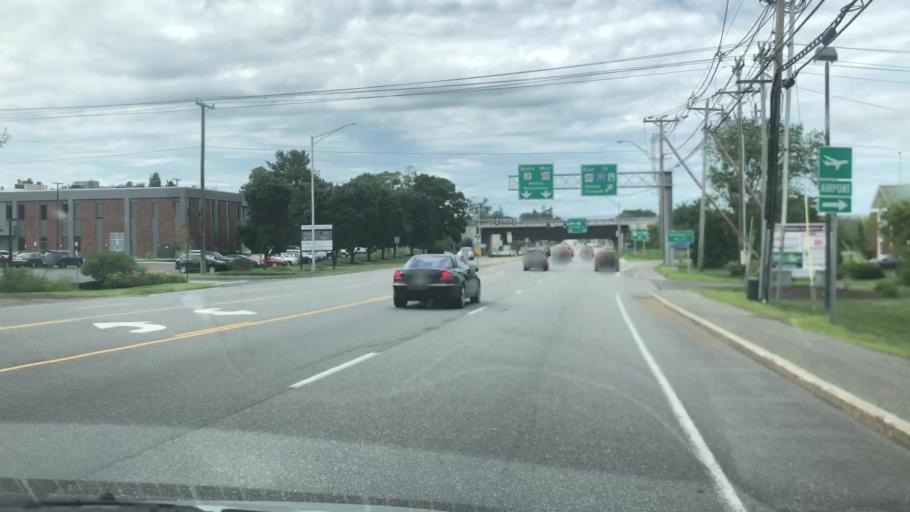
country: US
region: New Hampshire
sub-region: Hillsborough County
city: Bedford
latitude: 42.9488
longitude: -71.4768
